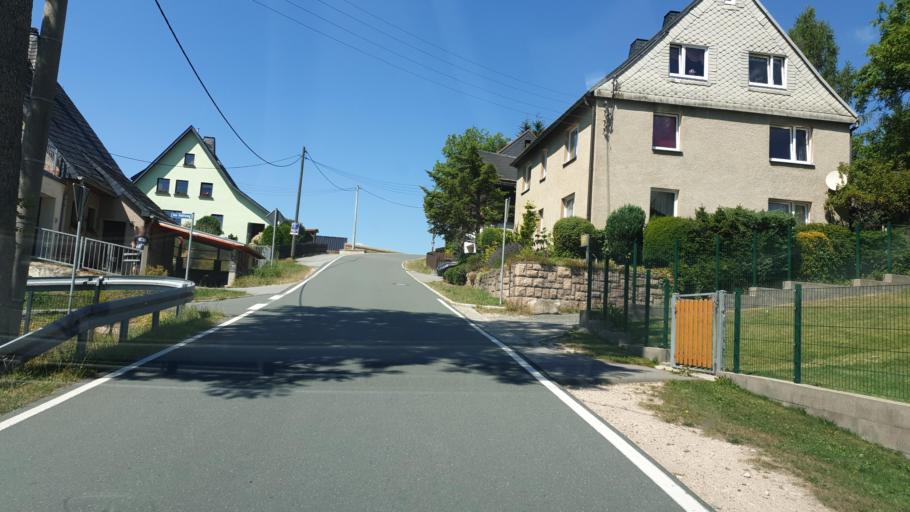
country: DE
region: Saxony
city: Sosa
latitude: 50.4973
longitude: 12.6572
